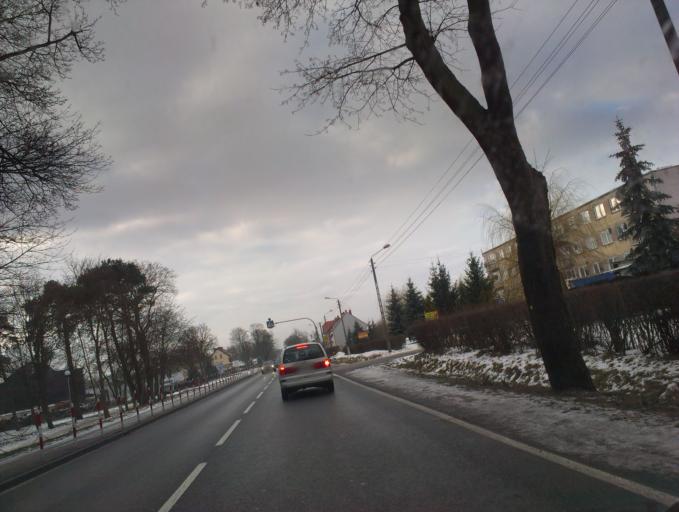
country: PL
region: Greater Poland Voivodeship
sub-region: Powiat zlotowski
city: Jastrowie
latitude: 53.4092
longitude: 16.7966
